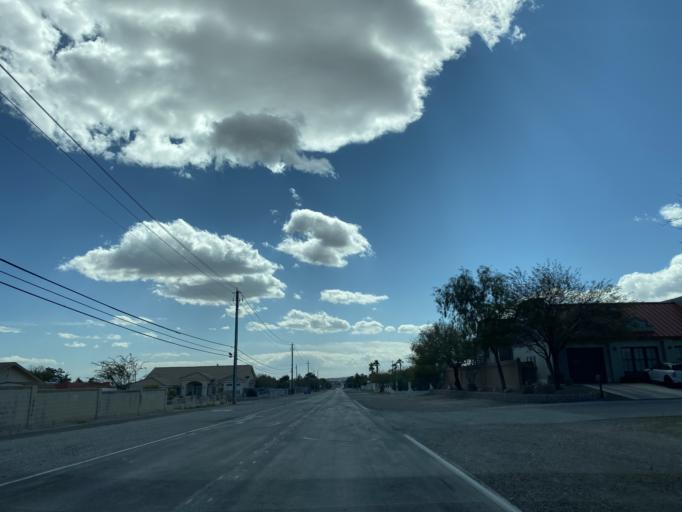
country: US
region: Nevada
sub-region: Clark County
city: Summerlin South
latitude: 36.2582
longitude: -115.2885
